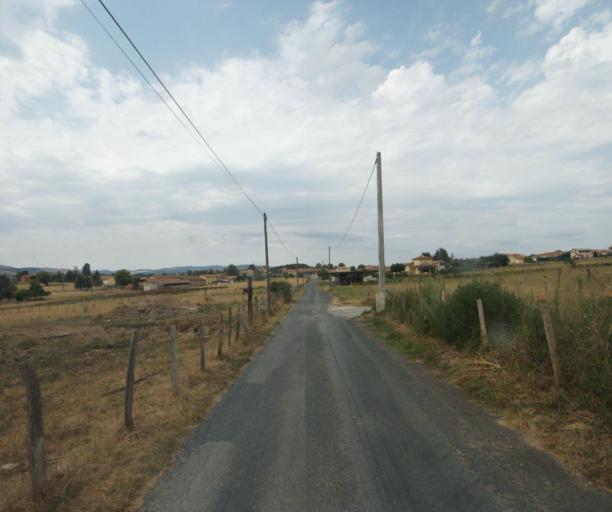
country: FR
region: Rhone-Alpes
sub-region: Departement du Rhone
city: Bully
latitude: 45.8738
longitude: 4.5574
